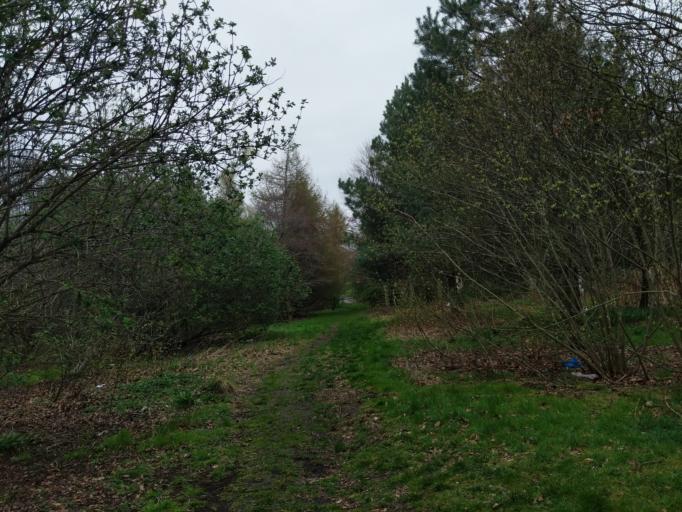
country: GB
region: Scotland
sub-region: Edinburgh
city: Colinton
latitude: 55.9285
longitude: -3.2863
